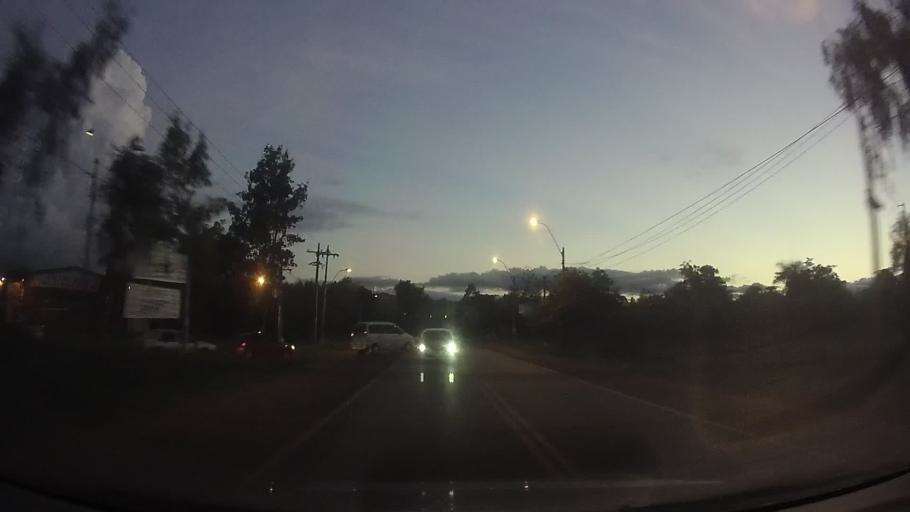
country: PY
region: Central
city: Itaugua
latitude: -25.3997
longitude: -57.3580
